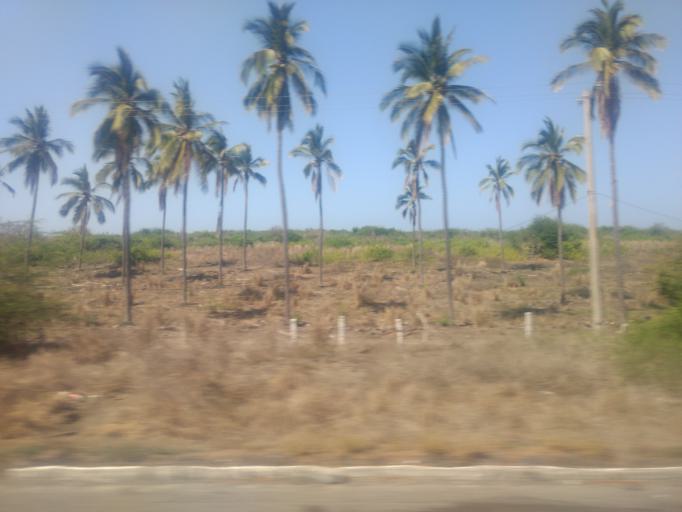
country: MX
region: Colima
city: Armeria
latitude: 18.9330
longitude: -104.0911
